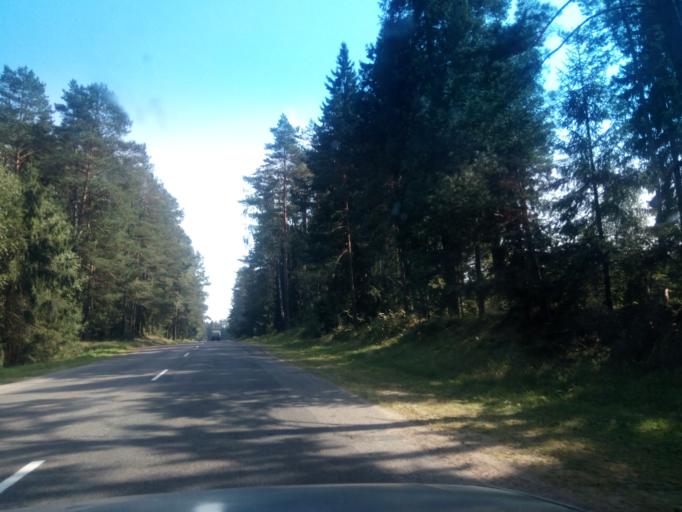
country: BY
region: Vitebsk
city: Vyerkhnyadzvinsk
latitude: 55.7944
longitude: 27.9647
